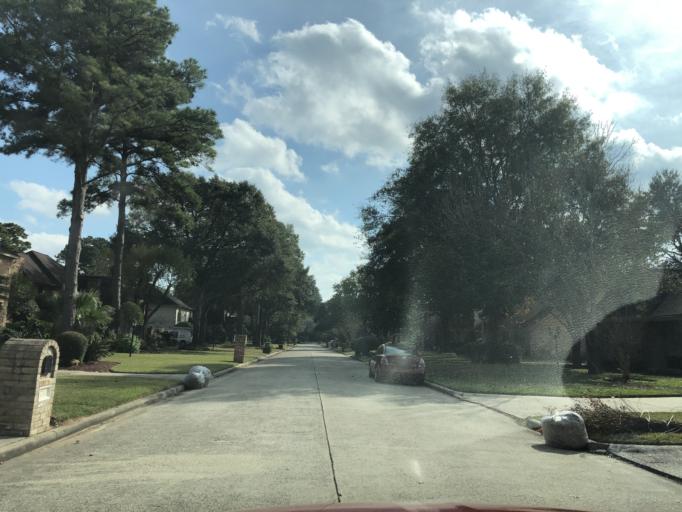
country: US
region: Texas
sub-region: Harris County
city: Tomball
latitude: 30.0244
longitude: -95.5445
